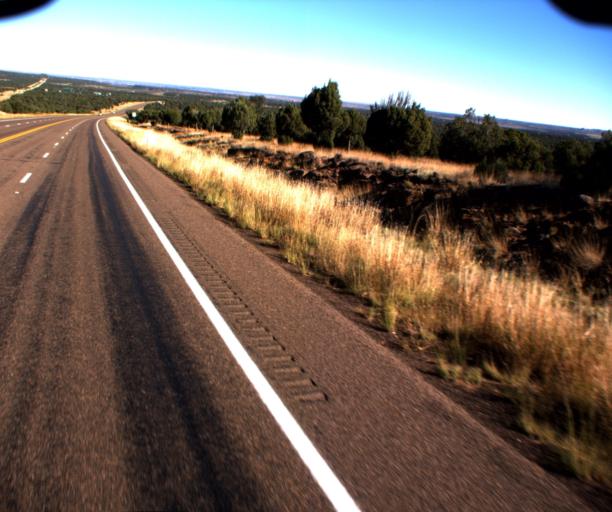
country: US
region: Arizona
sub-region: Navajo County
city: White Mountain Lake
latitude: 34.3419
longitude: -110.0512
